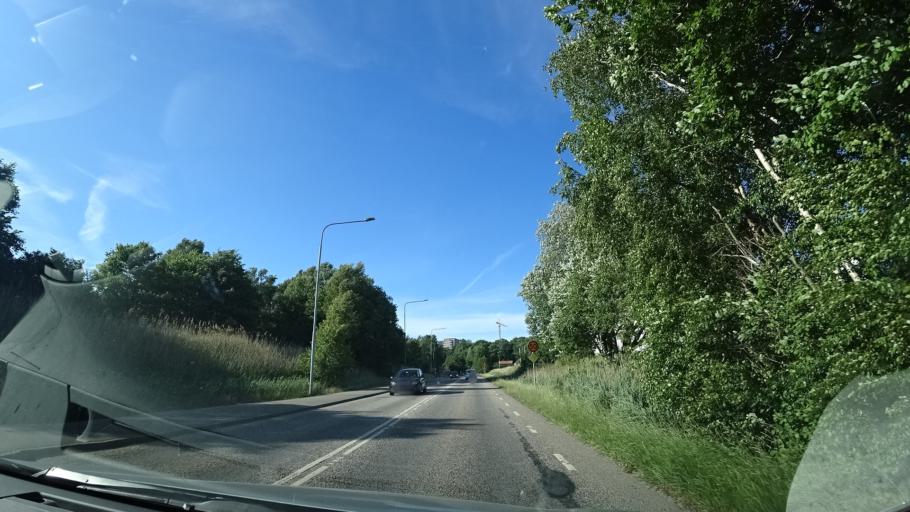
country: SE
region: Vaestra Goetaland
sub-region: Goteborg
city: Billdal
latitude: 57.5916
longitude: 11.9495
